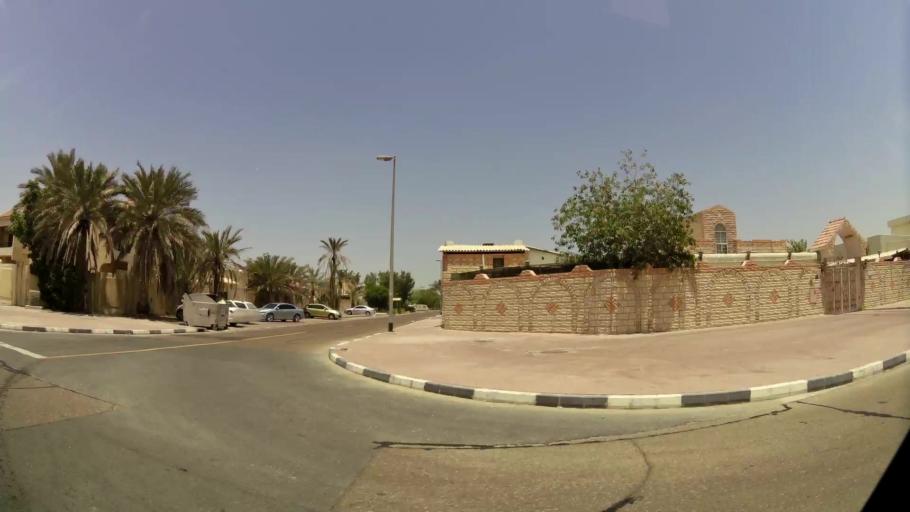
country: AE
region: Dubai
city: Dubai
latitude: 25.1951
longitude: 55.2517
